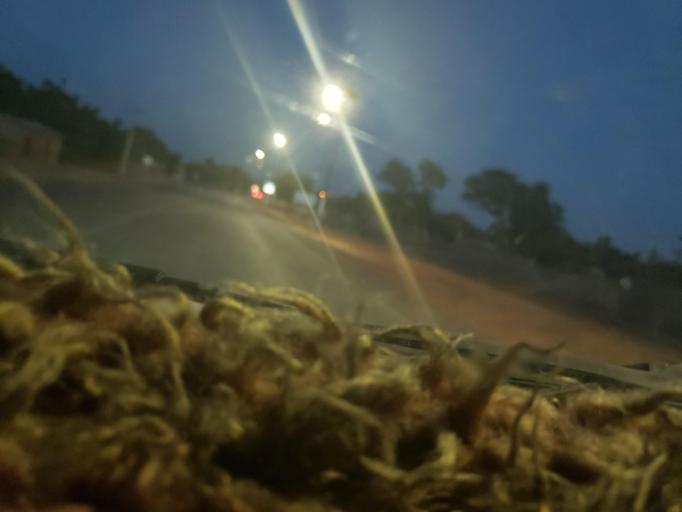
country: SN
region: Louga
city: Ndibene Dahra
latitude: 15.3840
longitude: -15.2388
